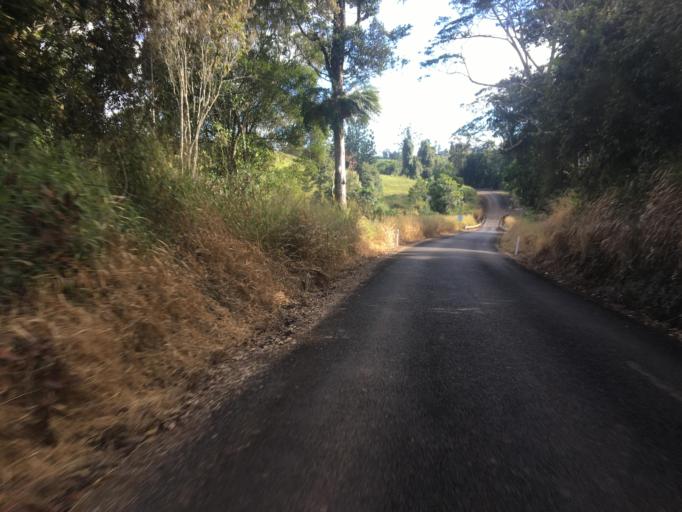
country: AU
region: Queensland
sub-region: Tablelands
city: Ravenshoe
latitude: -17.5710
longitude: 145.6089
